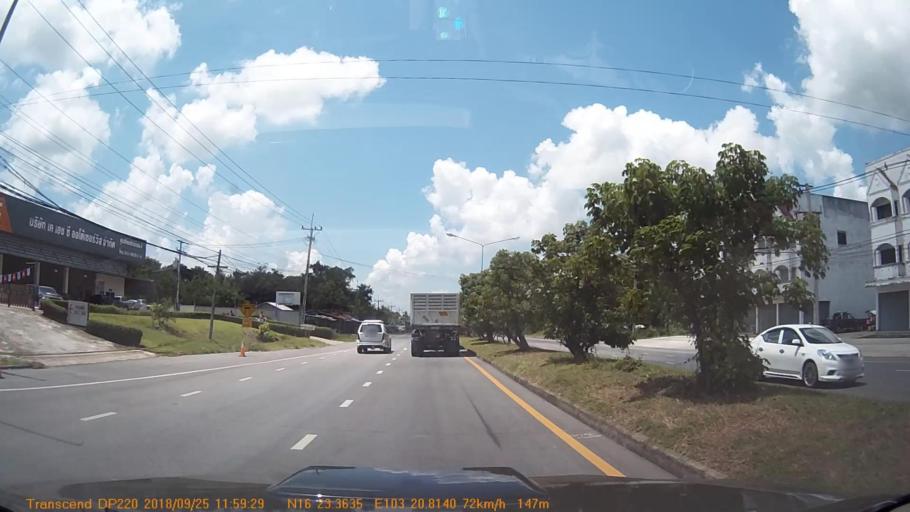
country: TH
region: Kalasin
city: Yang Talat
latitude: 16.3894
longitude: 103.3470
